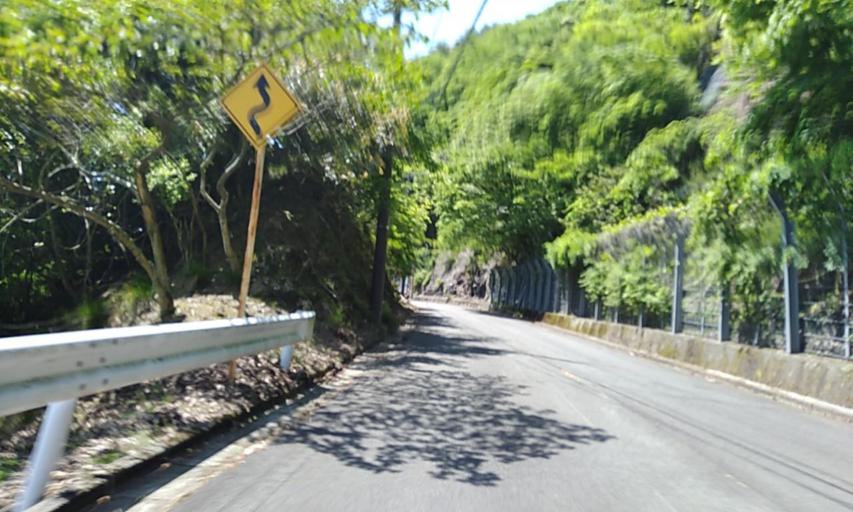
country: JP
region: Fukui
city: Obama
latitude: 35.5455
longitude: 135.7463
